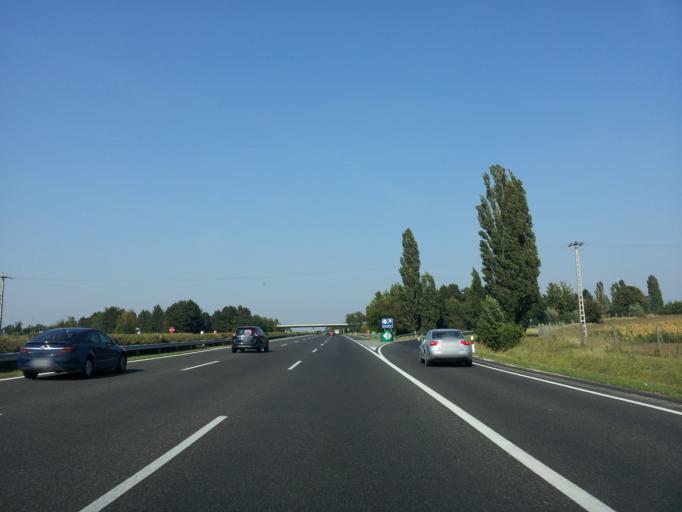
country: HU
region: Fejer
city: Szekesfehervar
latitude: 47.1463
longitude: 18.4337
